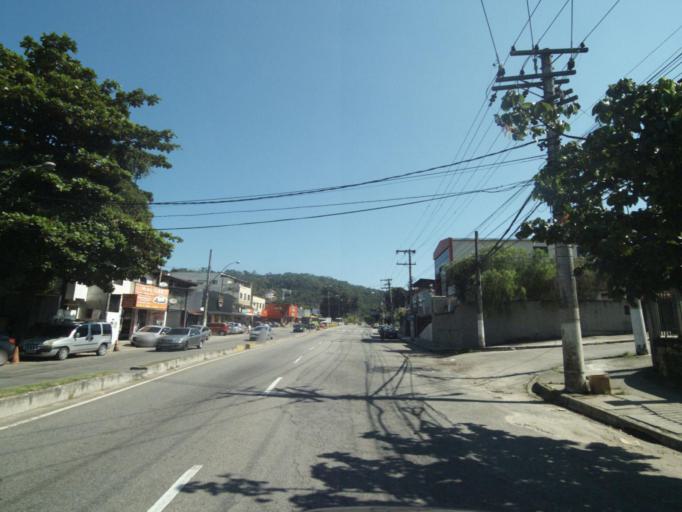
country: BR
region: Rio de Janeiro
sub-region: Niteroi
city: Niteroi
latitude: -22.8976
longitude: -43.0400
